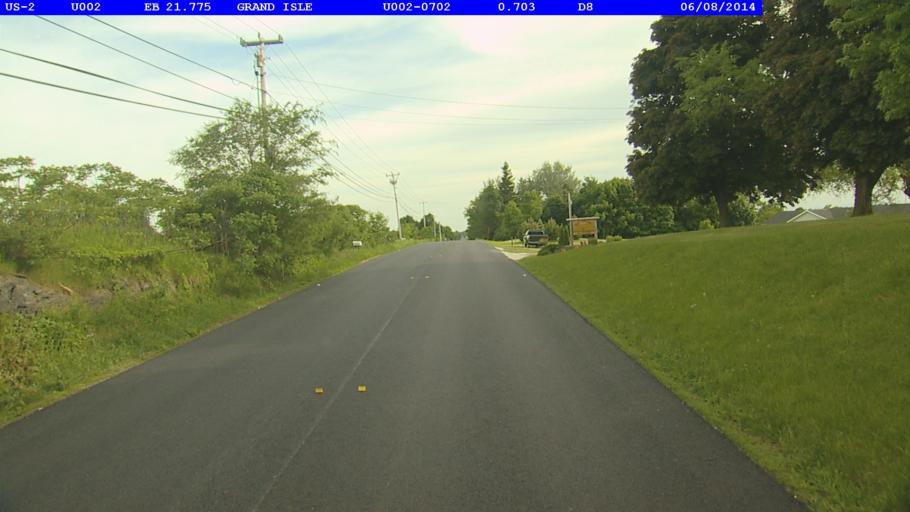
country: US
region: Vermont
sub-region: Grand Isle County
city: North Hero
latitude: 44.7572
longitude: -73.2863
